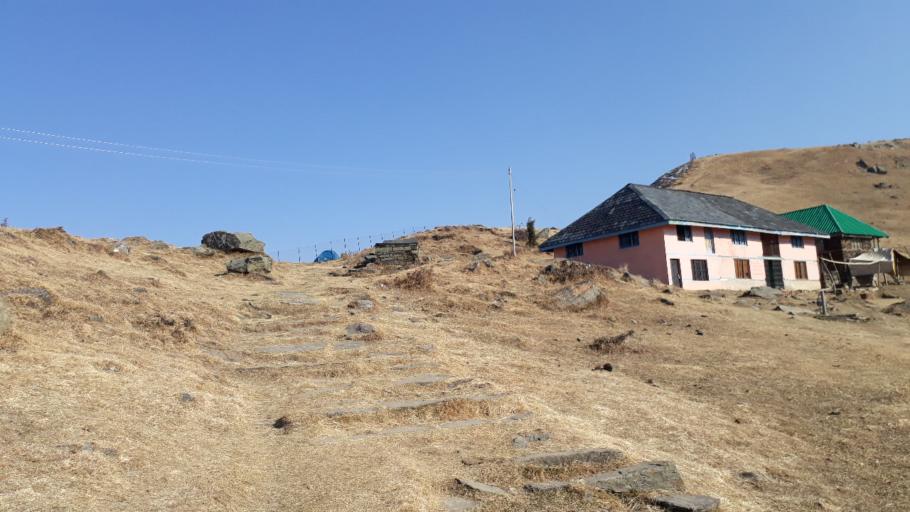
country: IN
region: Himachal Pradesh
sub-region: Mandi
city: Pandoh
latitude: 31.7549
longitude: 77.1030
